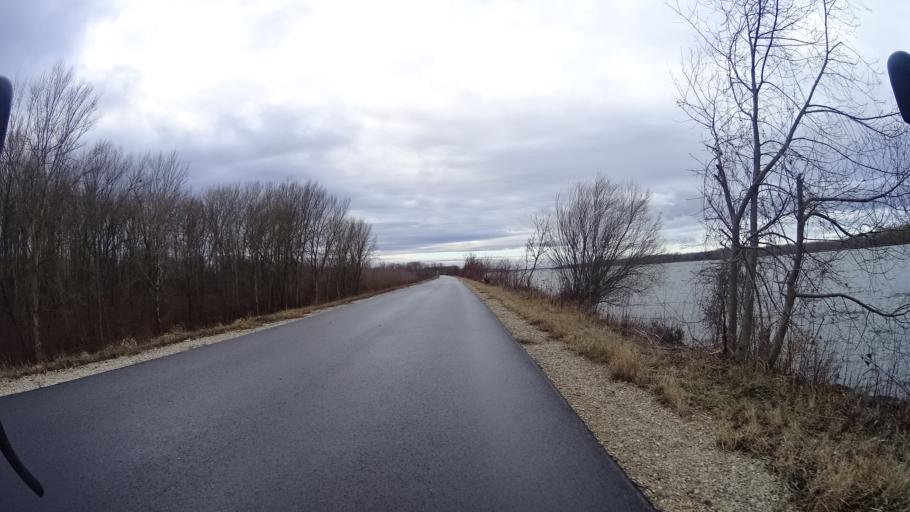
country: AT
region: Lower Austria
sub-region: Politischer Bezirk Tulln
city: Wordern
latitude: 48.3437
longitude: 16.1927
